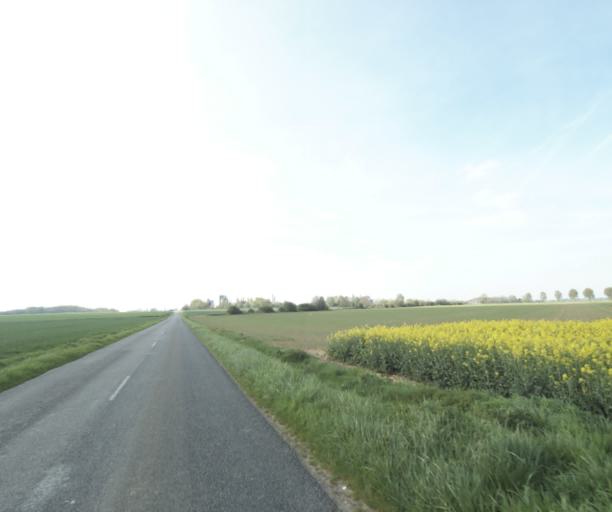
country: FR
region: Ile-de-France
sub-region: Departement de Seine-et-Marne
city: Nangis
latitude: 48.5726
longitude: 3.0122
